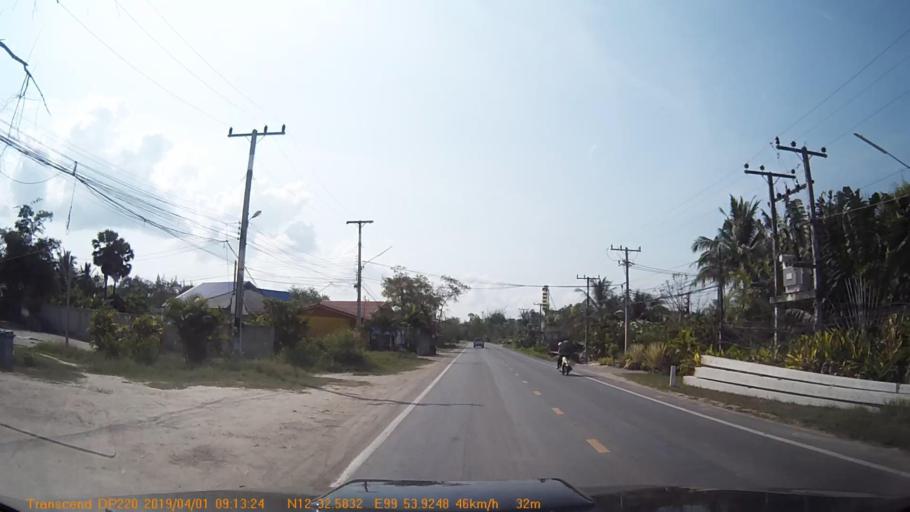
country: TH
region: Prachuap Khiri Khan
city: Hua Hin
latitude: 12.5429
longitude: 99.8989
